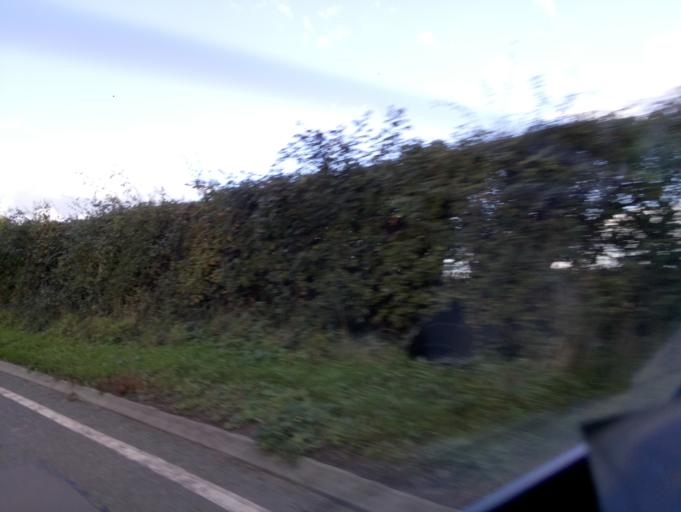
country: GB
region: England
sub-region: Herefordshire
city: Withington
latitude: 52.0668
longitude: -2.6320
